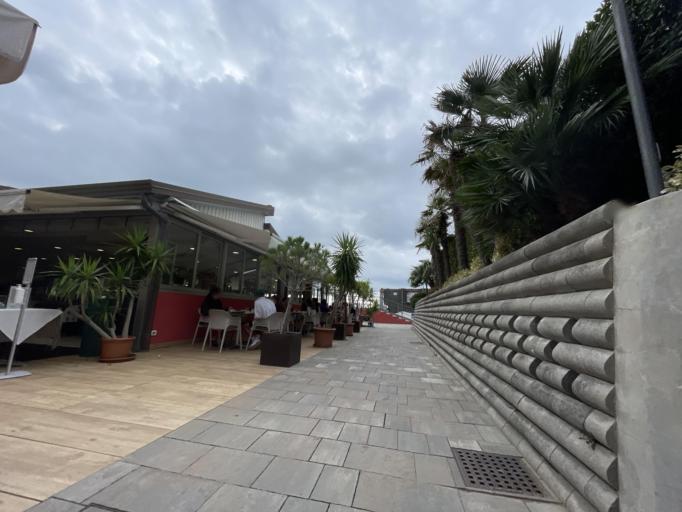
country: IT
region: Veneto
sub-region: Provincia di Venezia
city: Ca' Savio
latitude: 45.4526
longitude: 12.4910
